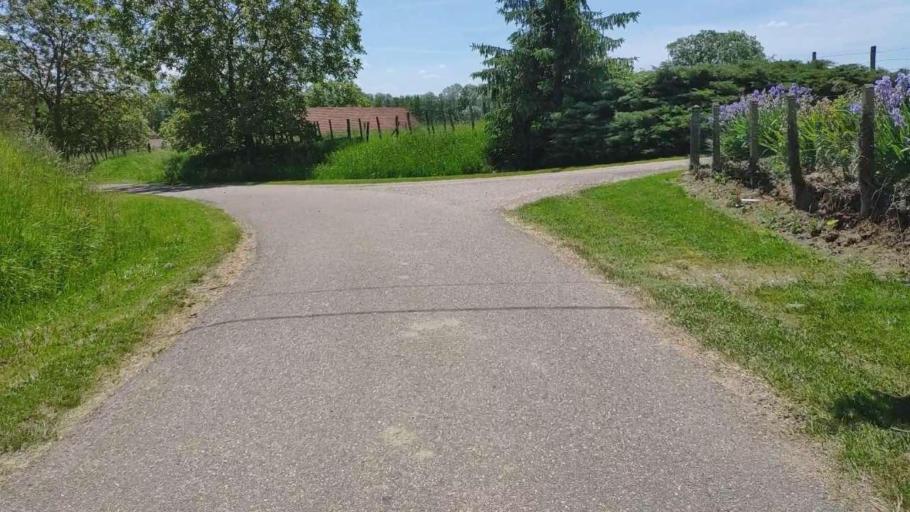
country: FR
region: Franche-Comte
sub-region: Departement du Jura
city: Bletterans
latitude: 46.7928
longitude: 5.3914
